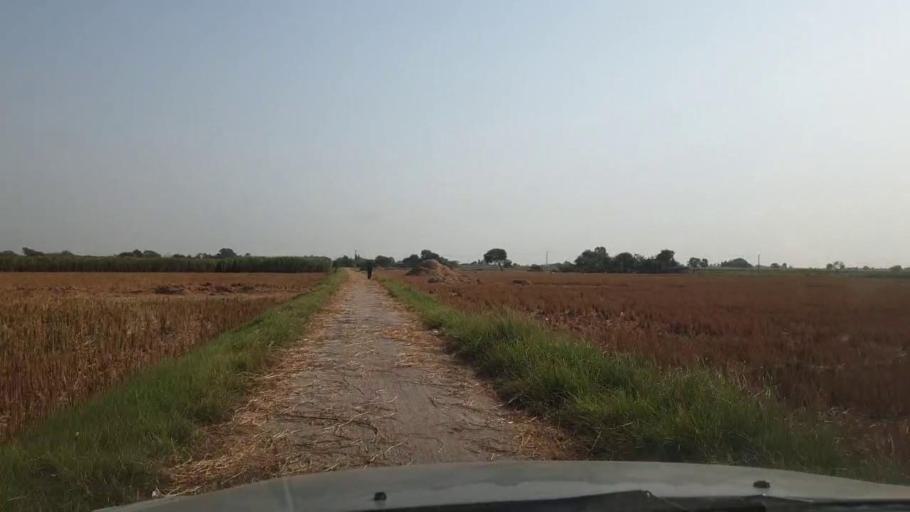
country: PK
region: Sindh
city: Bulri
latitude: 24.9183
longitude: 68.3128
